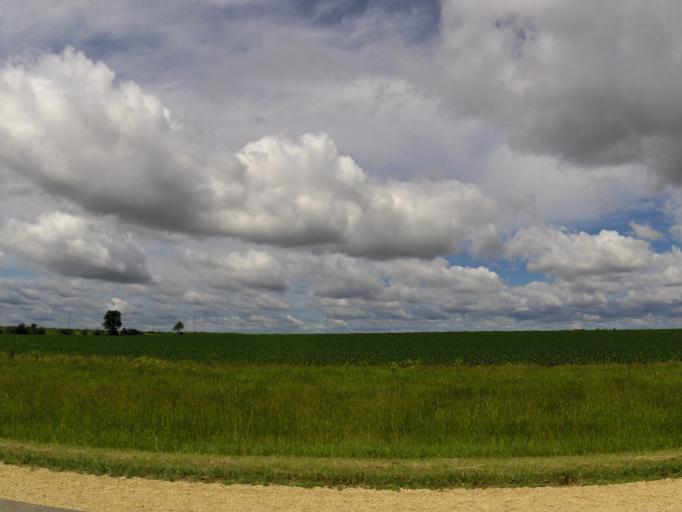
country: US
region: Minnesota
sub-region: Olmsted County
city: Stewartville
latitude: 43.8062
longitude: -92.4897
